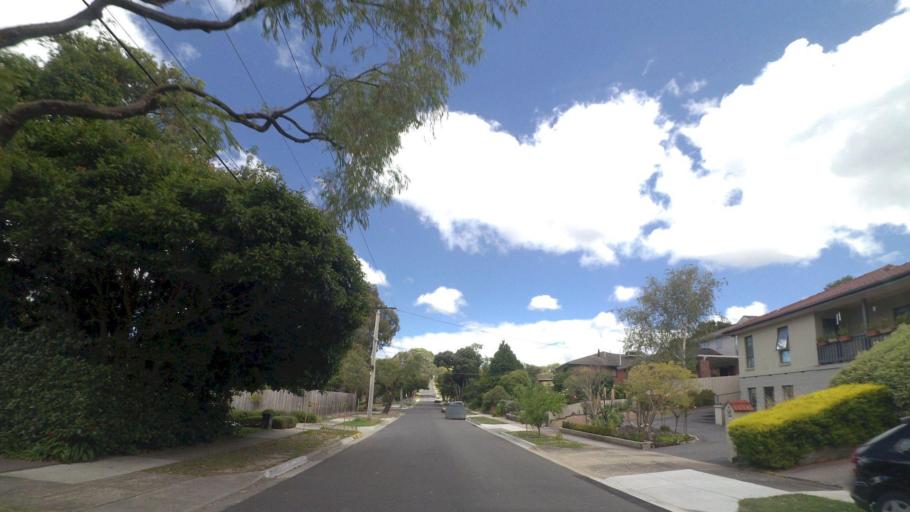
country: AU
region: Victoria
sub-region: Knox
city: Boronia
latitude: -37.8656
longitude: 145.2946
